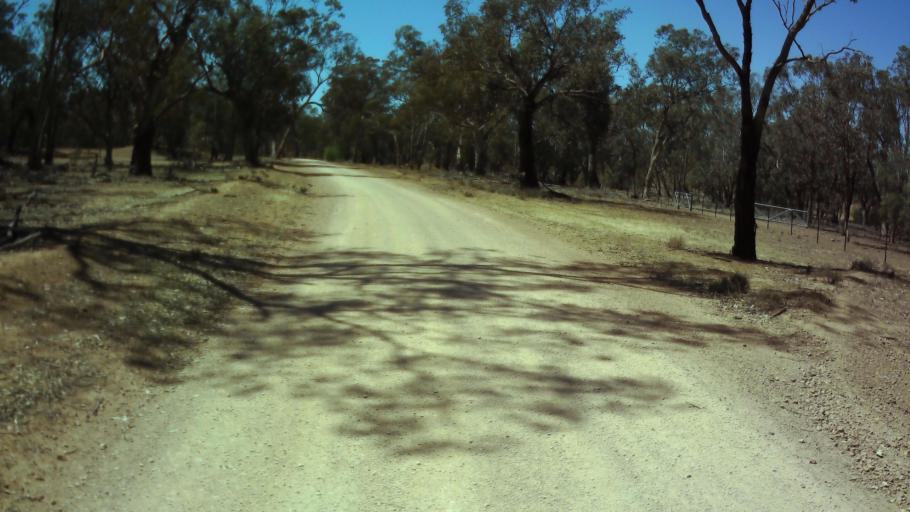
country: AU
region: New South Wales
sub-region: Weddin
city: Grenfell
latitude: -33.9377
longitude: 148.0777
